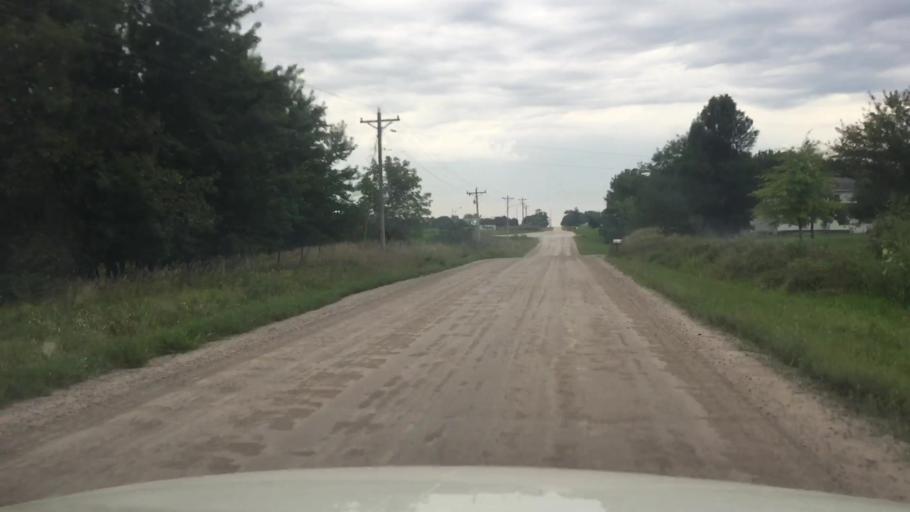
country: US
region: Iowa
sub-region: Story County
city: Huxley
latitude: 41.8879
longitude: -93.5810
